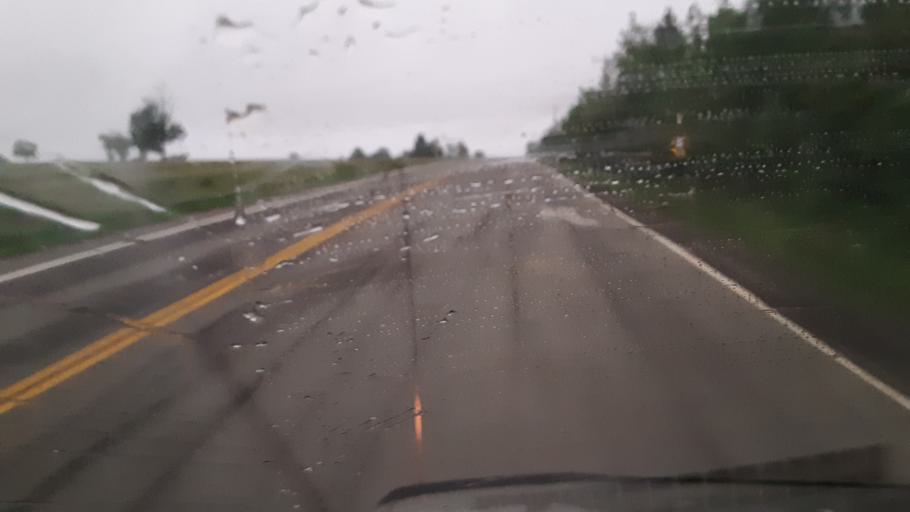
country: US
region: Maine
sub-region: Penobscot County
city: Patten
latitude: 46.0461
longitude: -68.4437
